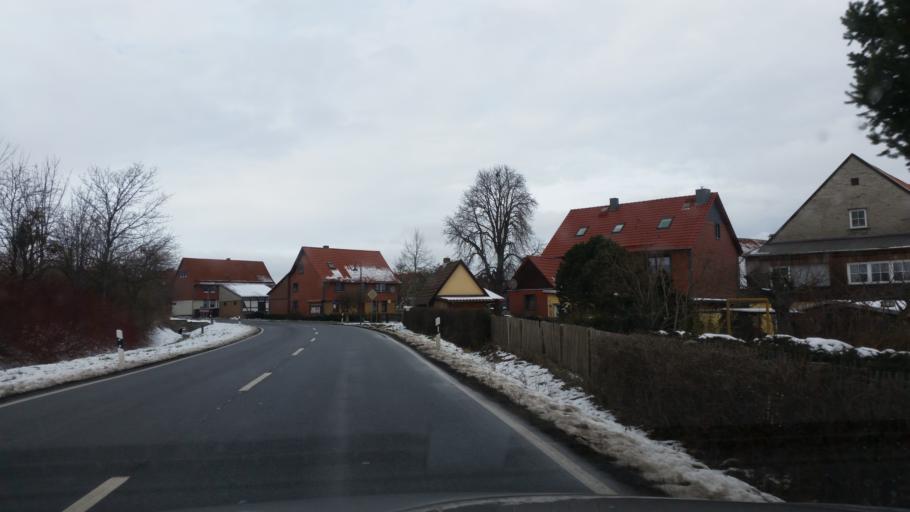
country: DE
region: Saxony-Anhalt
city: Drubeck
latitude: 51.8558
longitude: 10.7134
